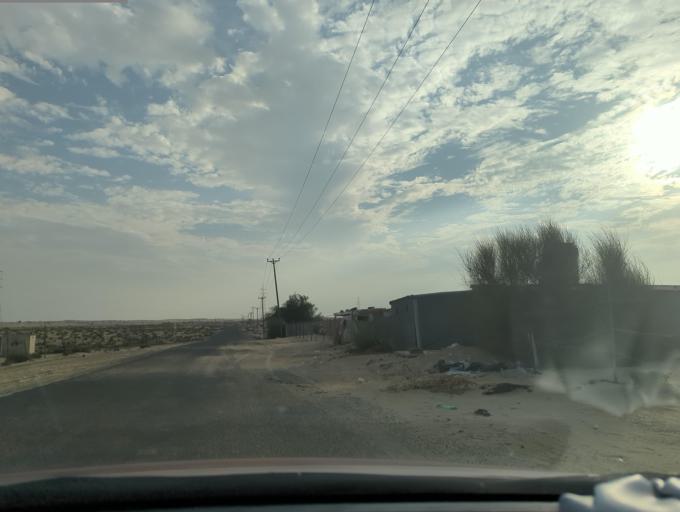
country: AE
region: Dubai
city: Dubai
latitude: 24.7193
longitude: 54.8735
